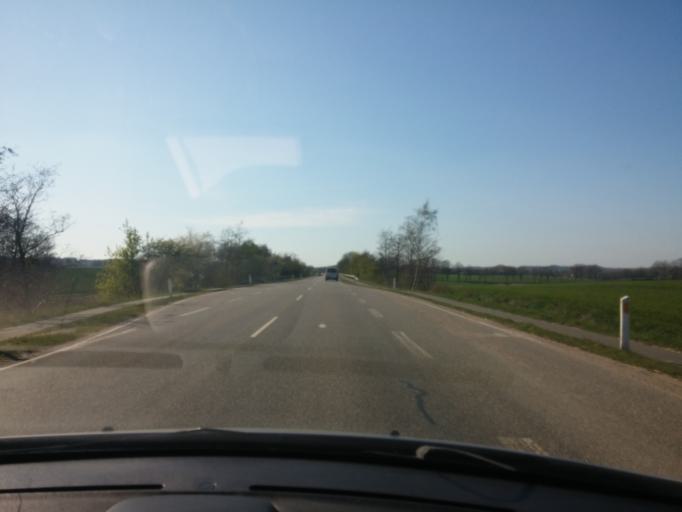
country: DK
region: Central Jutland
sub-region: Odder Kommune
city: Odder
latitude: 55.9601
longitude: 10.1815
